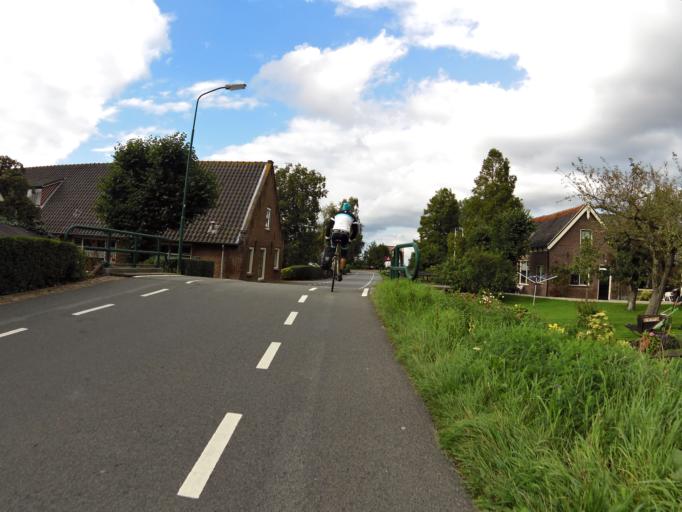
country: NL
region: North Holland
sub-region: Gemeente Wijdemeren
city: Oud-Loosdrecht
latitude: 52.1720
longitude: 5.0794
